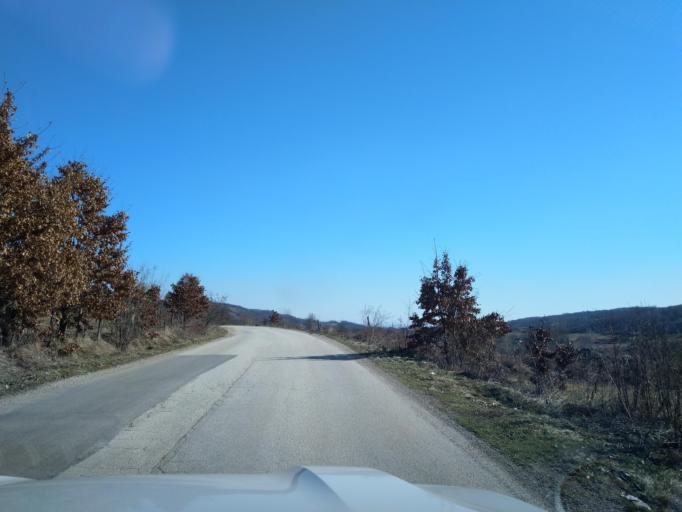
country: RS
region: Central Serbia
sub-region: Zlatiborski Okrug
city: Kosjeric
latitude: 43.9317
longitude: 19.8914
